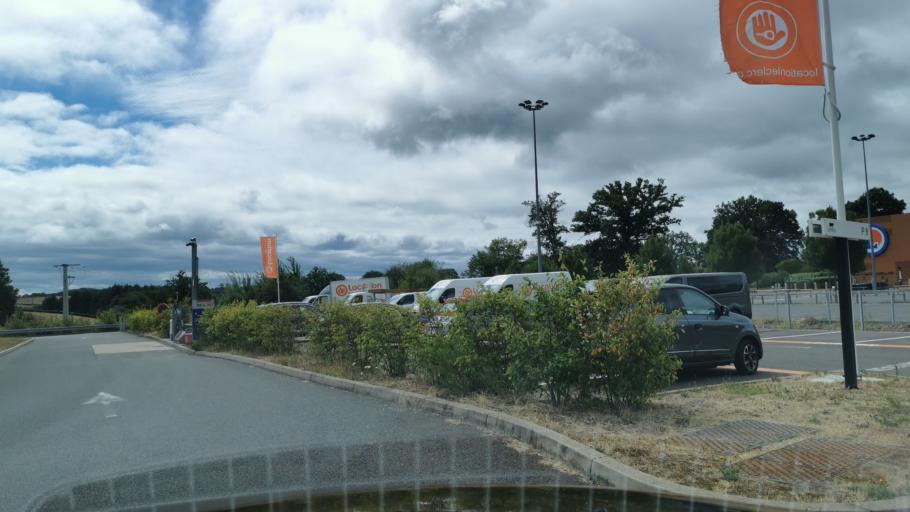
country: FR
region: Bourgogne
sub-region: Departement de Saone-et-Loire
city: Le Breuil
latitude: 46.8054
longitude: 4.4773
